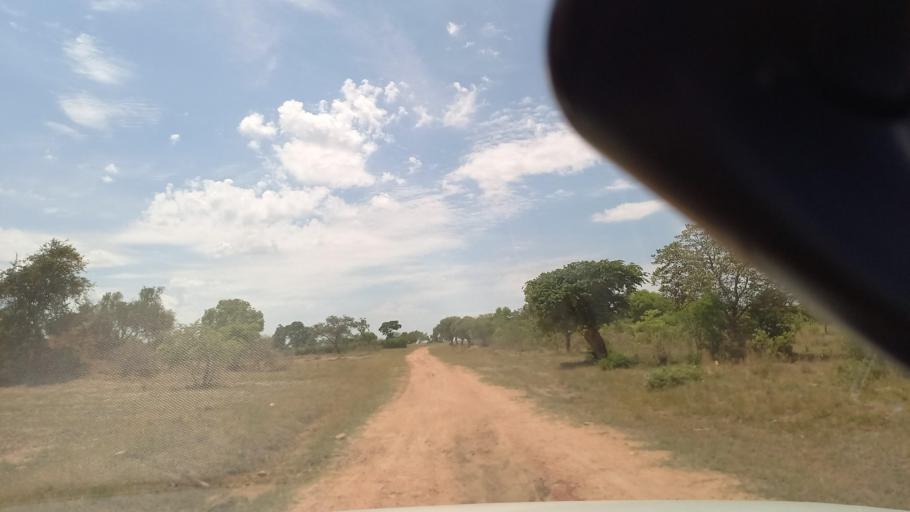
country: ZM
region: Southern
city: Mazabuka
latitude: -16.1489
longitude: 27.7772
